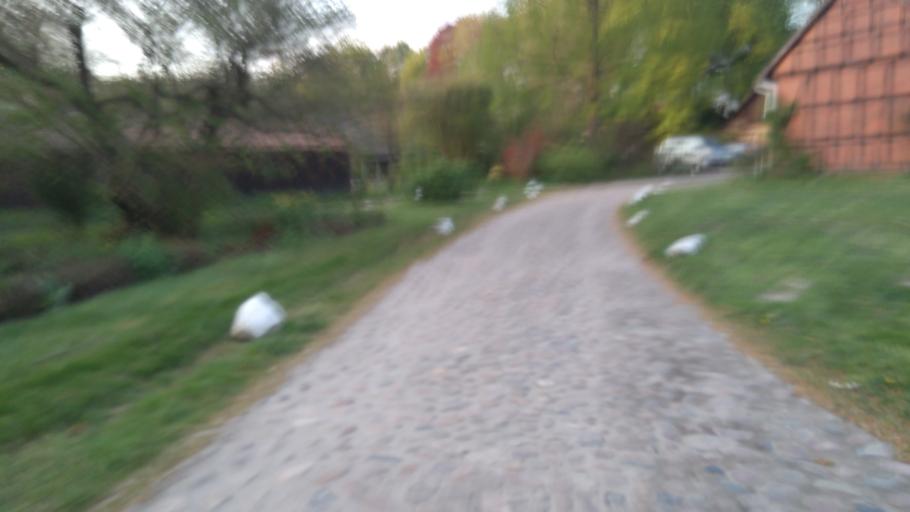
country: DE
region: Lower Saxony
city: Bliedersdorf
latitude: 53.4979
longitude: 9.5554
